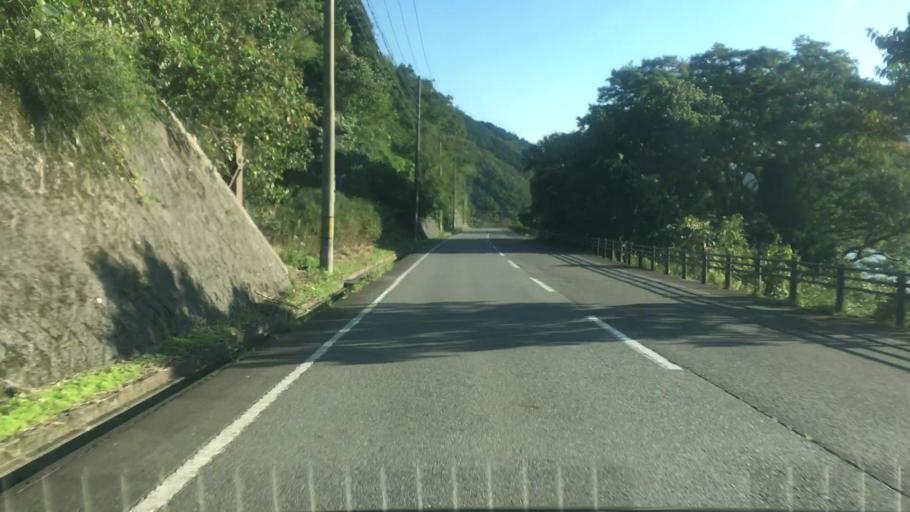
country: JP
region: Hyogo
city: Toyooka
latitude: 35.6009
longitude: 134.8060
